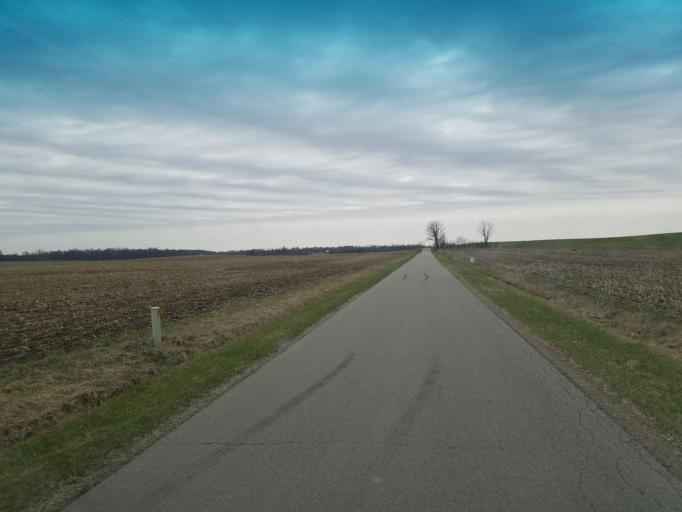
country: US
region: Ohio
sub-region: Crawford County
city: Bucyrus
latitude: 40.8445
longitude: -82.9307
